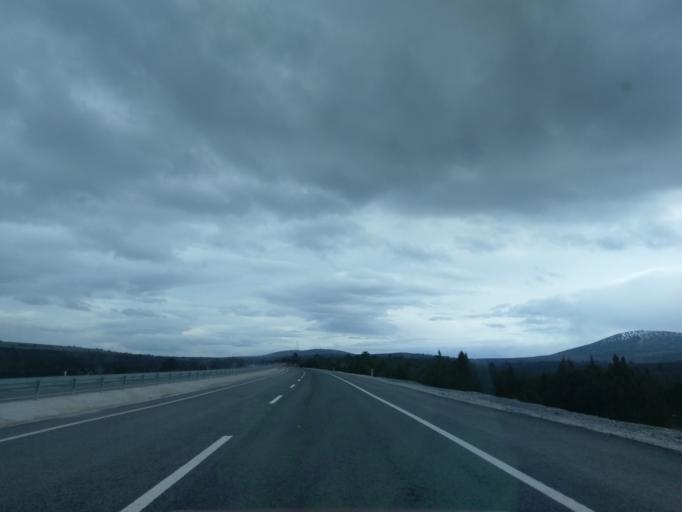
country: TR
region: Kuetahya
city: Cavdarhisar
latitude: 39.2224
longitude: 29.7351
